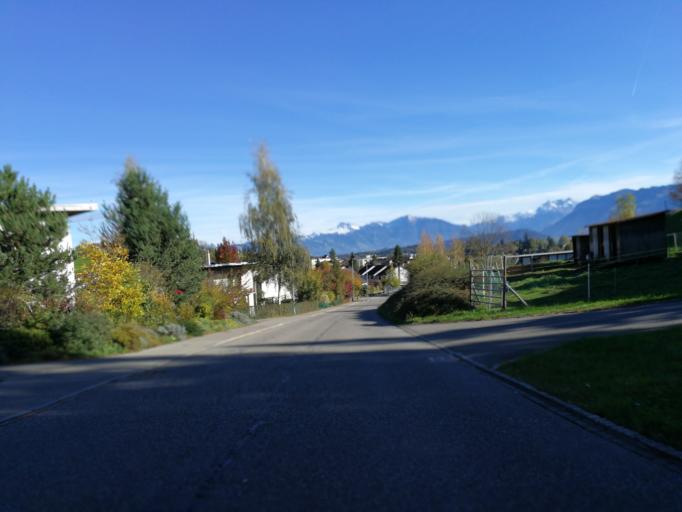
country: CH
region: Saint Gallen
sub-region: Wahlkreis See-Gaster
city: Rapperswil
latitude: 47.2428
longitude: 8.8159
